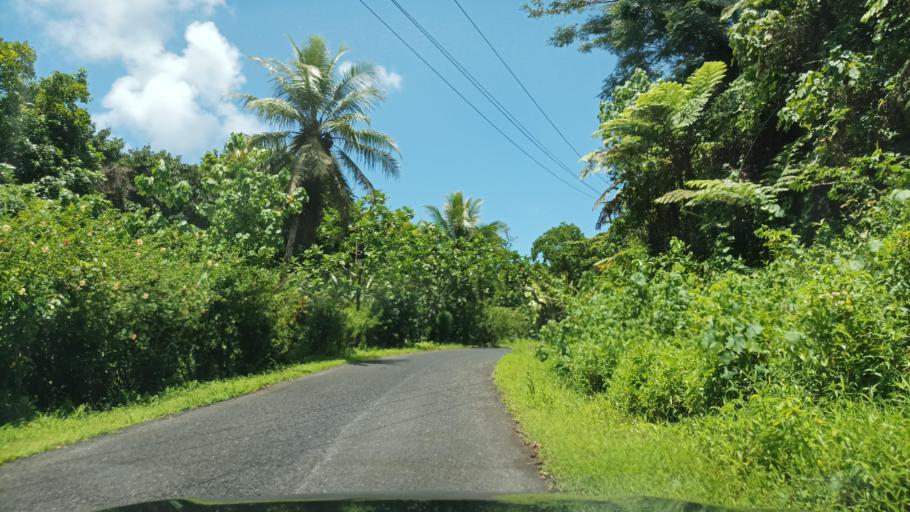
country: FM
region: Pohnpei
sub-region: Madolenihm Municipality
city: Madolenihm Municipality Government
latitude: 6.8656
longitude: 158.2910
